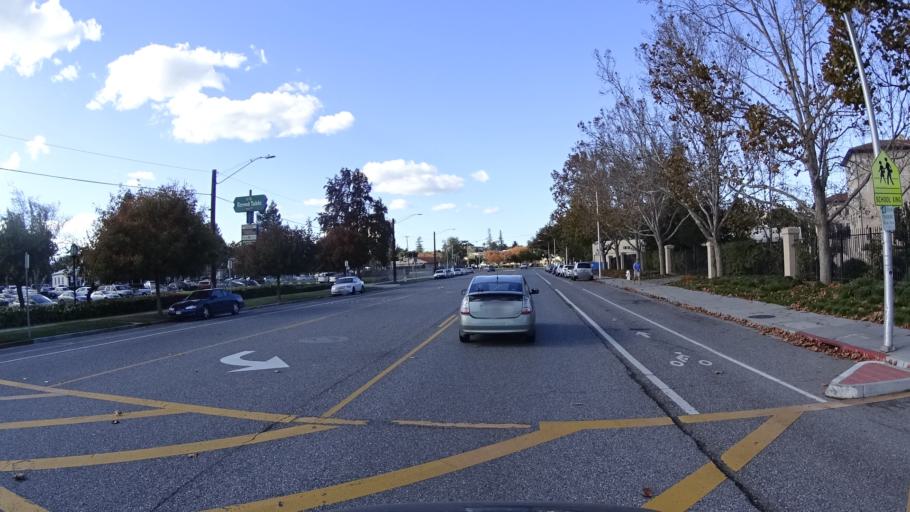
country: US
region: California
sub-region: Santa Clara County
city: Santa Clara
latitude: 37.3458
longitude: -121.9361
